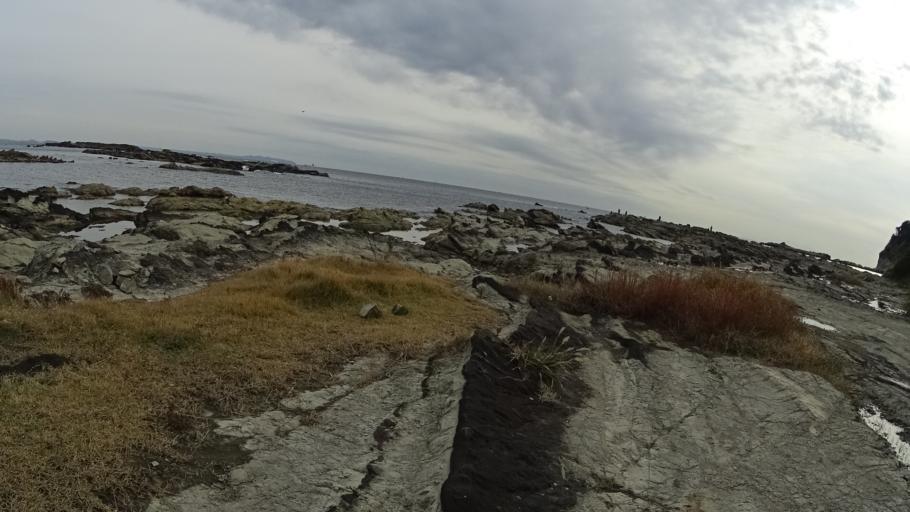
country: JP
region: Kanagawa
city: Miura
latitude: 35.1404
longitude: 139.6597
